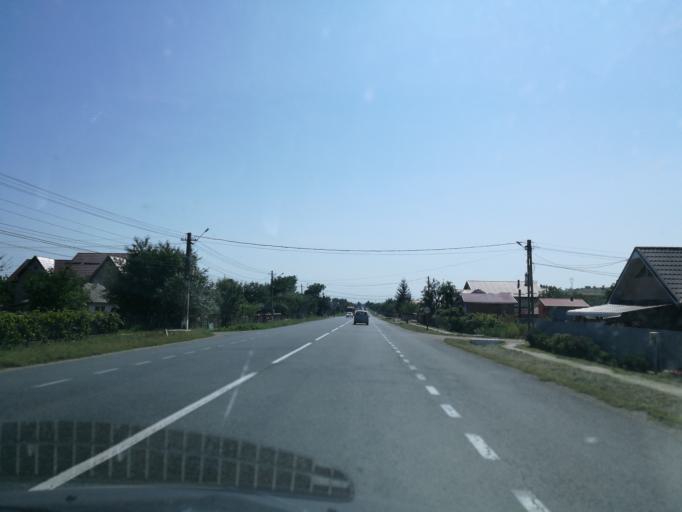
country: RO
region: Bacau
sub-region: Comuna Racaciuni
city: Racaciuni
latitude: 46.3277
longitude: 27.0109
